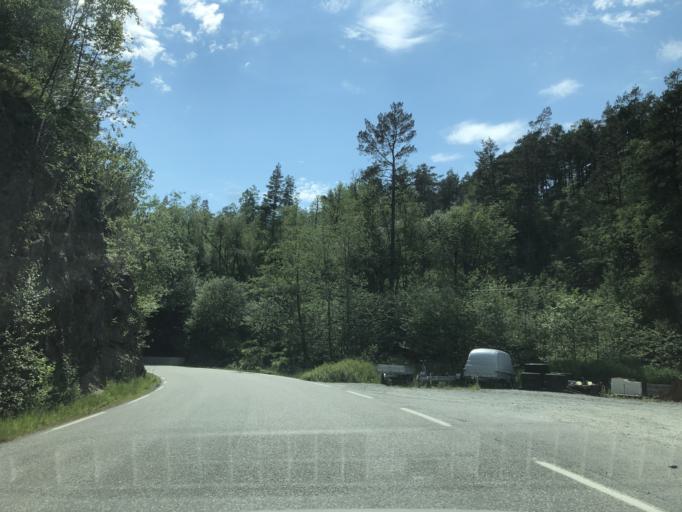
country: NO
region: Hordaland
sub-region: Jondal
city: Jondal
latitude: 60.2945
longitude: 6.2382
